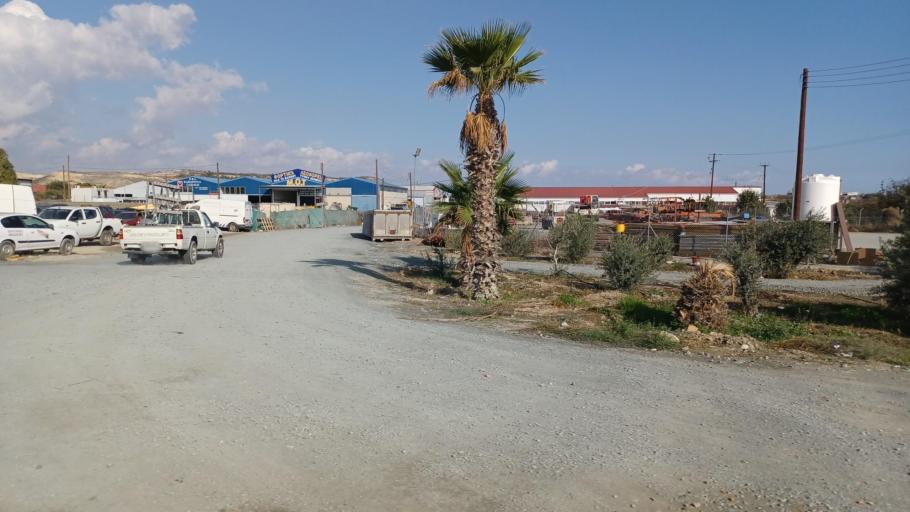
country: CY
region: Larnaka
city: Livadia
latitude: 34.9666
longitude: 33.6282
